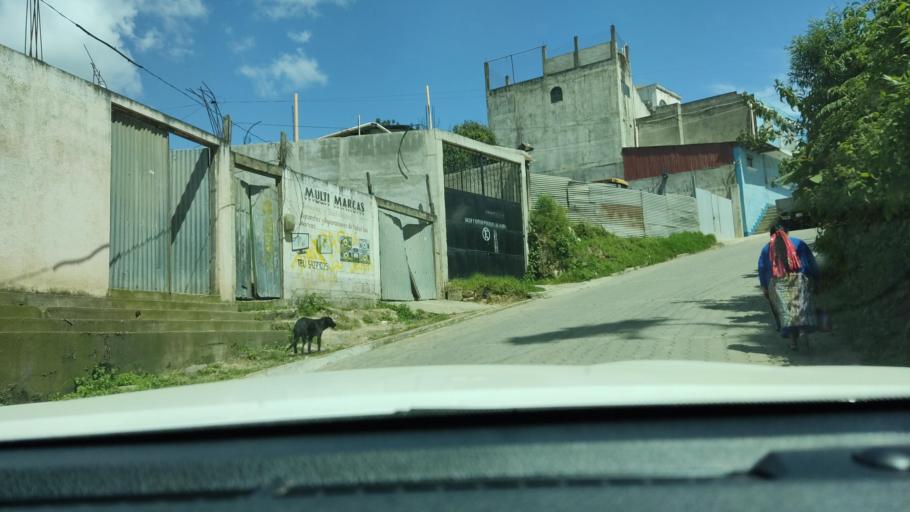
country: GT
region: Chimaltenango
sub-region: Municipio de San Juan Comalapa
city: Comalapa
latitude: 14.7443
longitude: -90.8878
